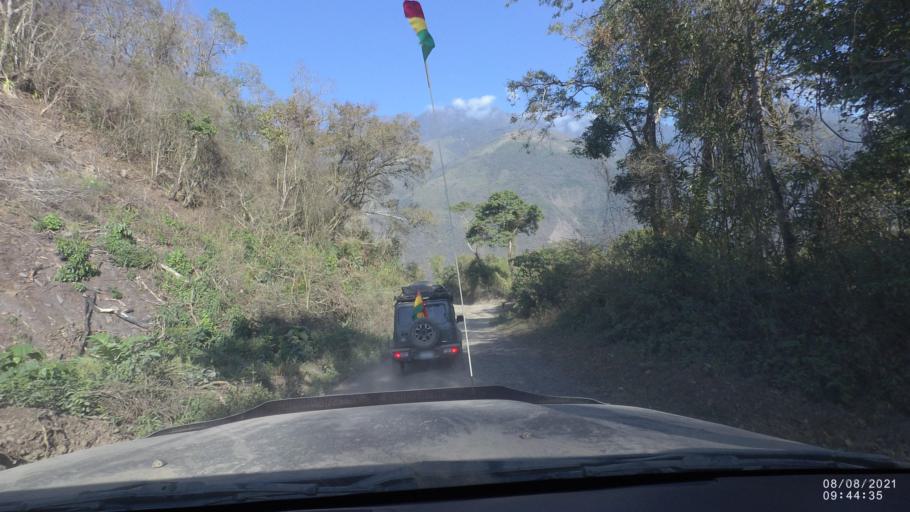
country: BO
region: La Paz
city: Quime
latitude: -16.6017
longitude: -66.7240
